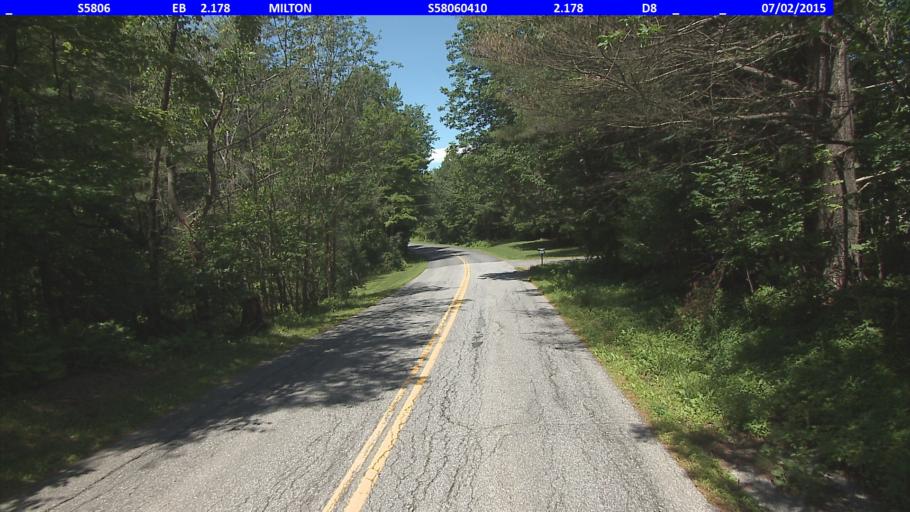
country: US
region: Vermont
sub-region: Chittenden County
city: Milton
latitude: 44.6633
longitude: -73.1524
